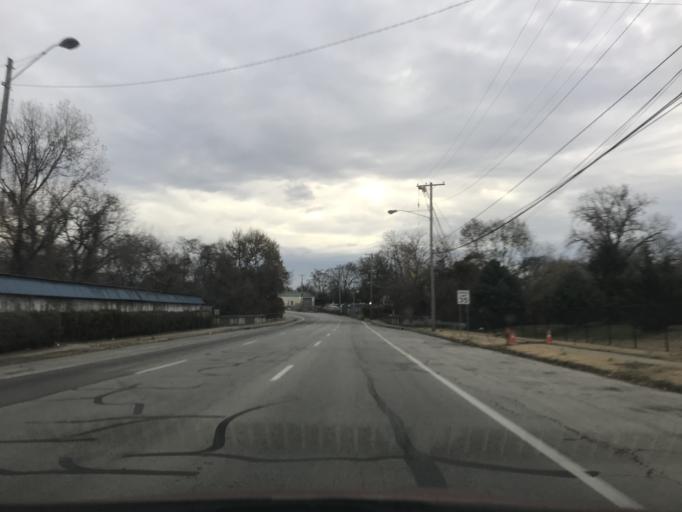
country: US
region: Indiana
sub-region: Clark County
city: Jeffersonville
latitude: 38.2536
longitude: -85.7285
